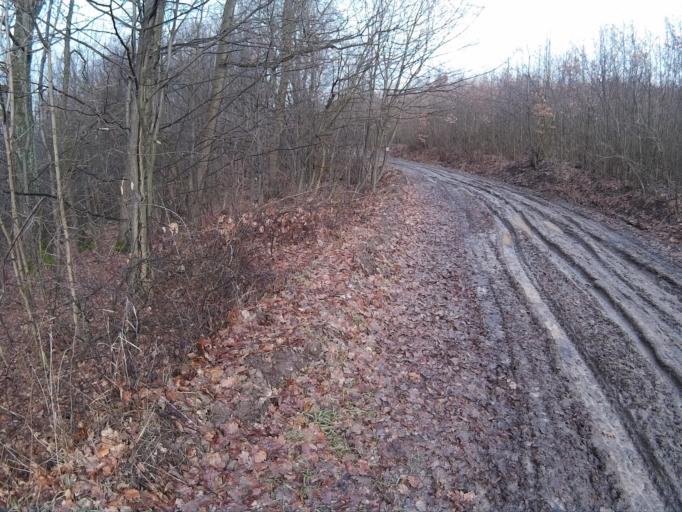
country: HU
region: Borsod-Abauj-Zemplen
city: Tolcsva
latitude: 48.3624
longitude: 21.4835
